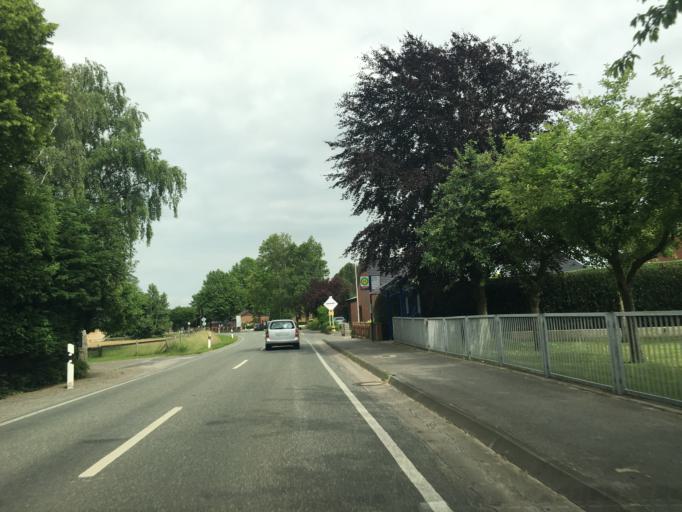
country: DE
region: North Rhine-Westphalia
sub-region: Regierungsbezirk Munster
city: Horstmar
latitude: 52.1062
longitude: 7.3072
